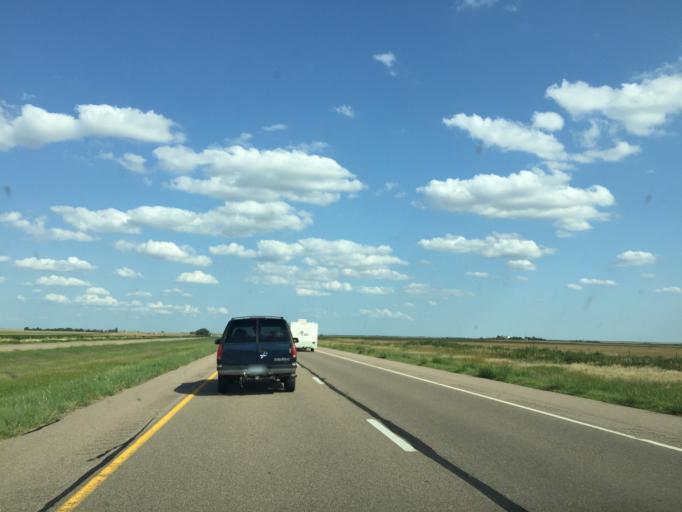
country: US
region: Kansas
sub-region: Trego County
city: WaKeeney
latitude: 39.0298
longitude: -100.1820
